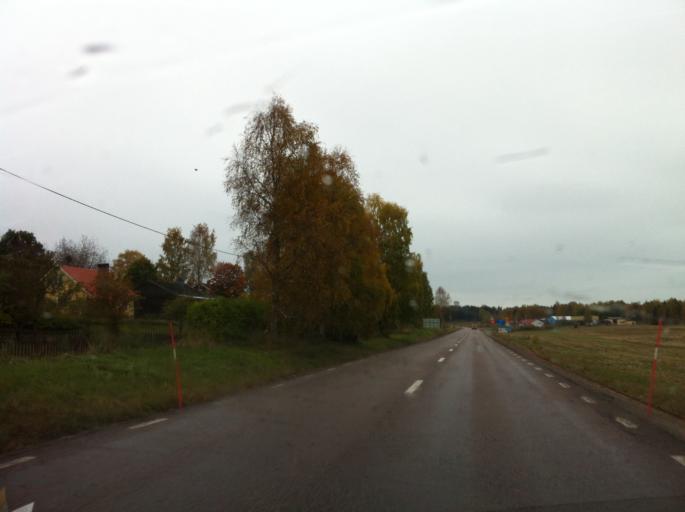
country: SE
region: Dalarna
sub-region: Ludvika Kommun
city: Grangesberg
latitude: 60.2509
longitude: 14.9796
